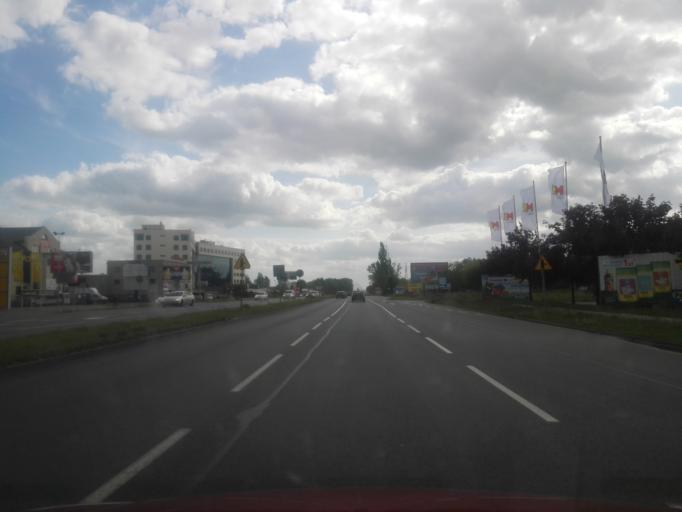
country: PL
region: Masovian Voivodeship
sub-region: Powiat wolominski
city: Zabki
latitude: 52.3025
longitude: 21.0881
